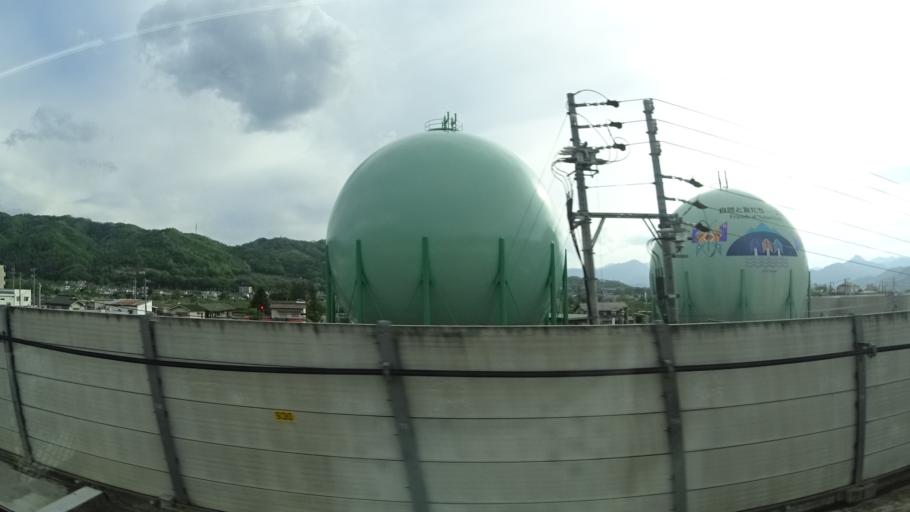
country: JP
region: Nagano
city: Ueda
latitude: 36.4028
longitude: 138.2410
